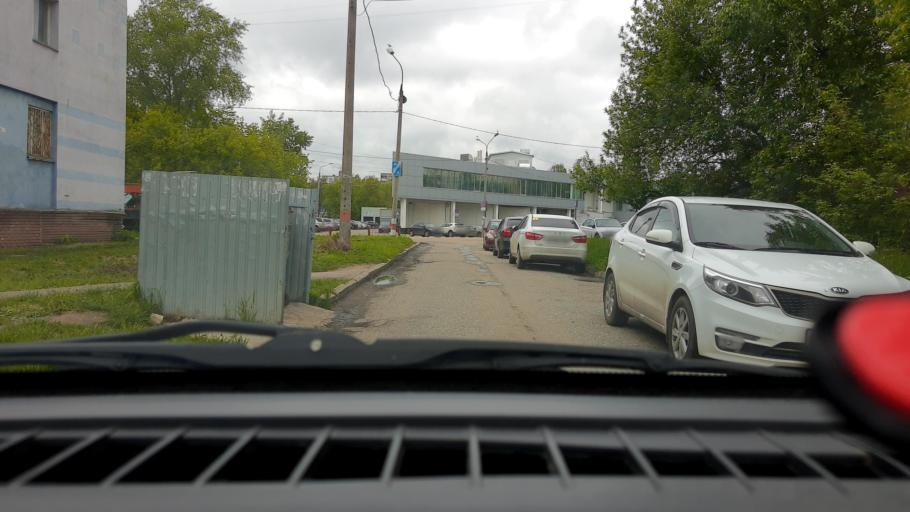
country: RU
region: Nizjnij Novgorod
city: Gorbatovka
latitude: 56.2581
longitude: 43.8758
